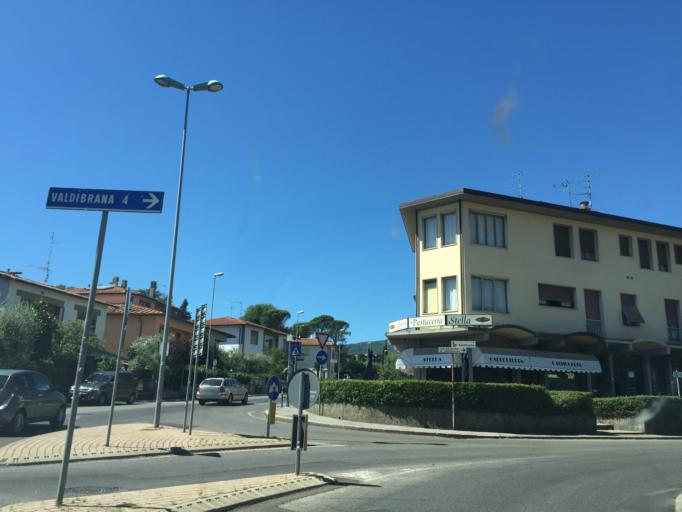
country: IT
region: Tuscany
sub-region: Provincia di Pistoia
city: Pistoia
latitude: 43.9443
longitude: 10.9111
